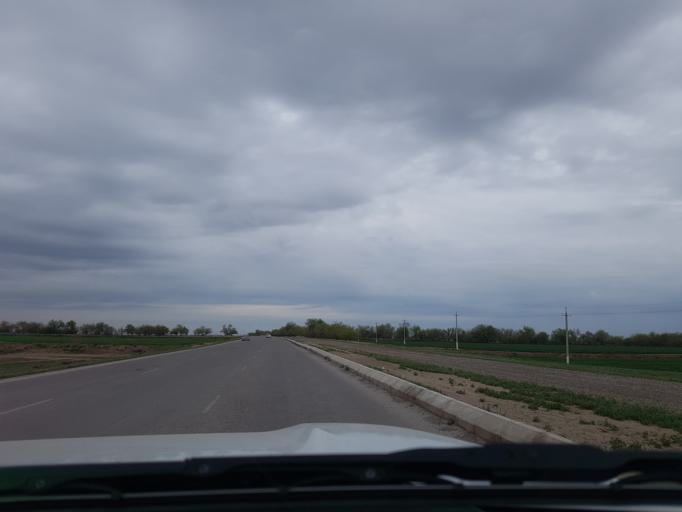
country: TM
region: Mary
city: Bayramaly
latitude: 37.5976
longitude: 62.2081
